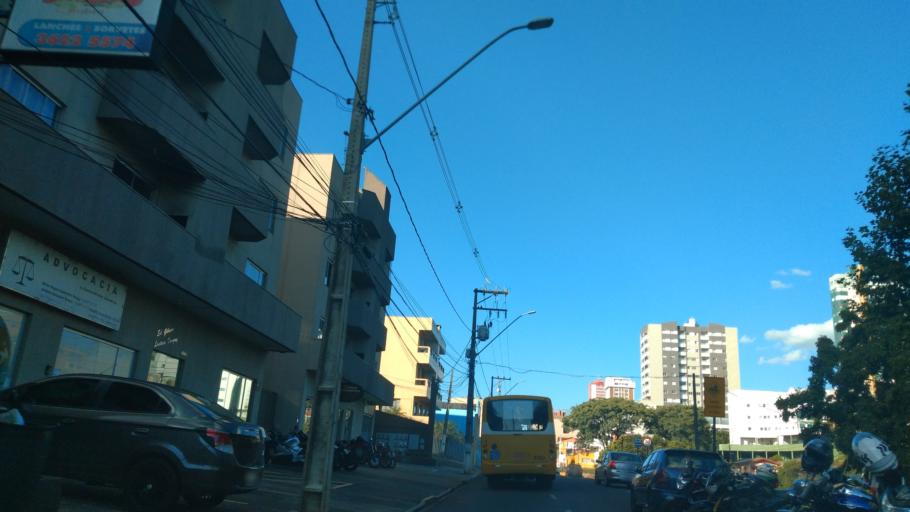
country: BR
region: Parana
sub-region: Guarapuava
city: Guarapuava
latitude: -25.3976
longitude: -51.4722
